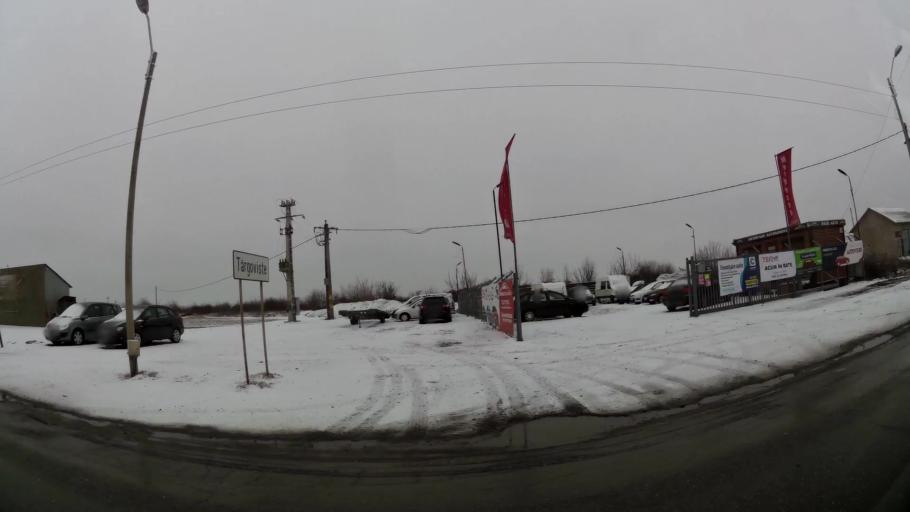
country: RO
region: Dambovita
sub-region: Comuna Ulmi
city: Ulmi
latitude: 44.9048
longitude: 25.4951
